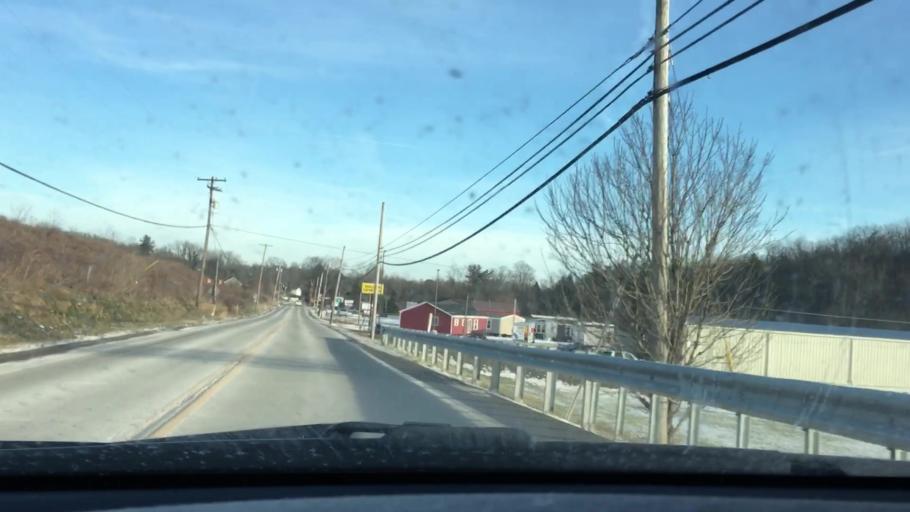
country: US
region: Pennsylvania
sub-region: Washington County
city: Gastonville
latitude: 40.2705
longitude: -80.0190
